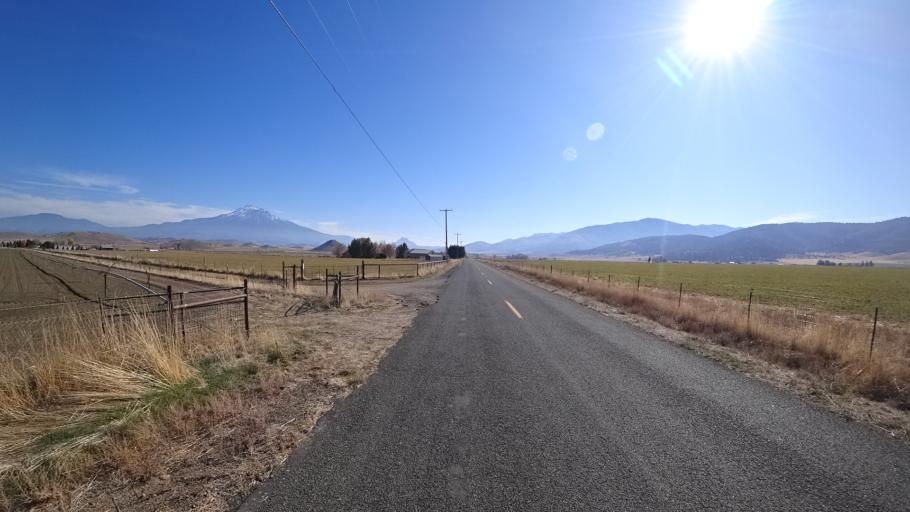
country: US
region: California
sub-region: Siskiyou County
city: Montague
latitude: 41.5483
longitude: -122.5426
